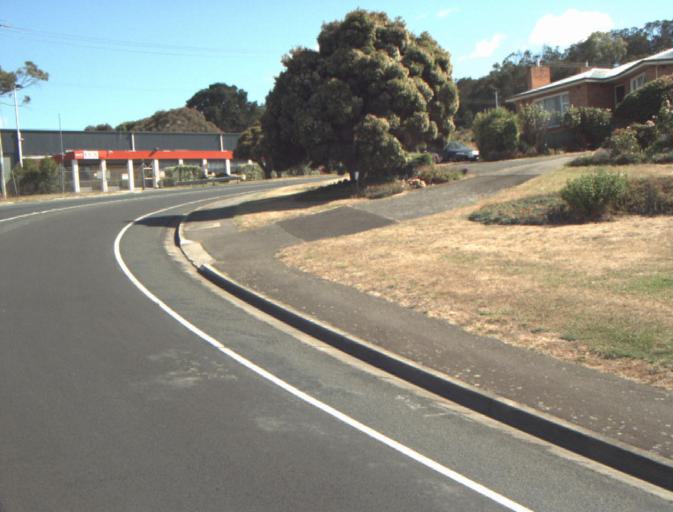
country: AU
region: Tasmania
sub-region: Launceston
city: Newstead
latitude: -41.4314
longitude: 147.1730
